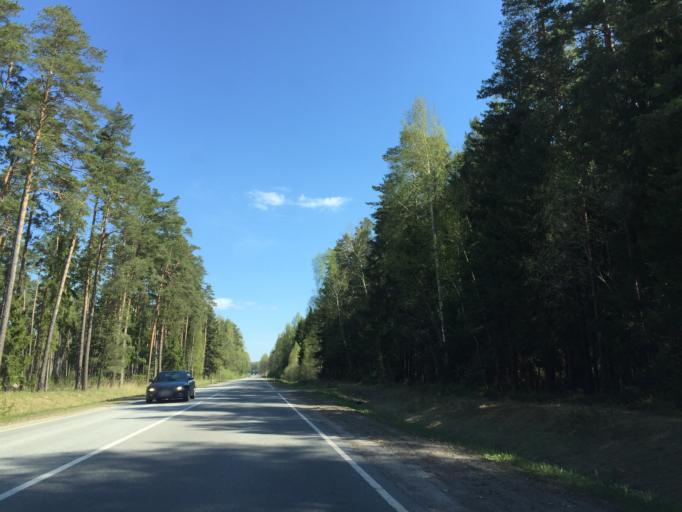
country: LV
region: Saulkrastu
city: Saulkrasti
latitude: 57.3248
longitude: 24.4302
